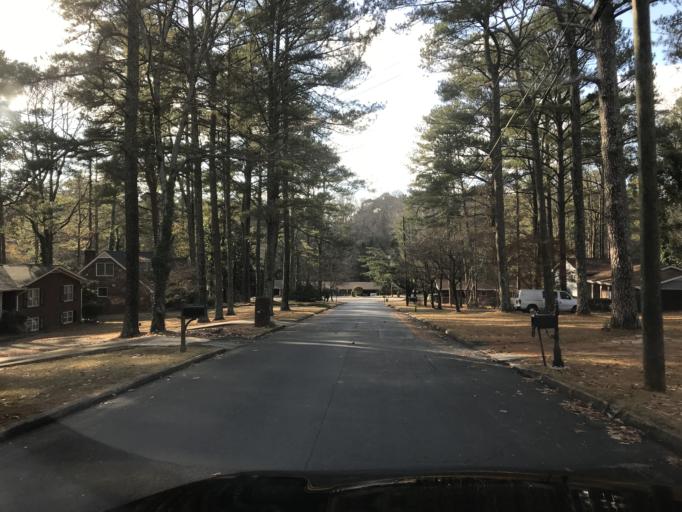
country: US
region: Georgia
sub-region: Fulton County
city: College Park
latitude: 33.6325
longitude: -84.4751
